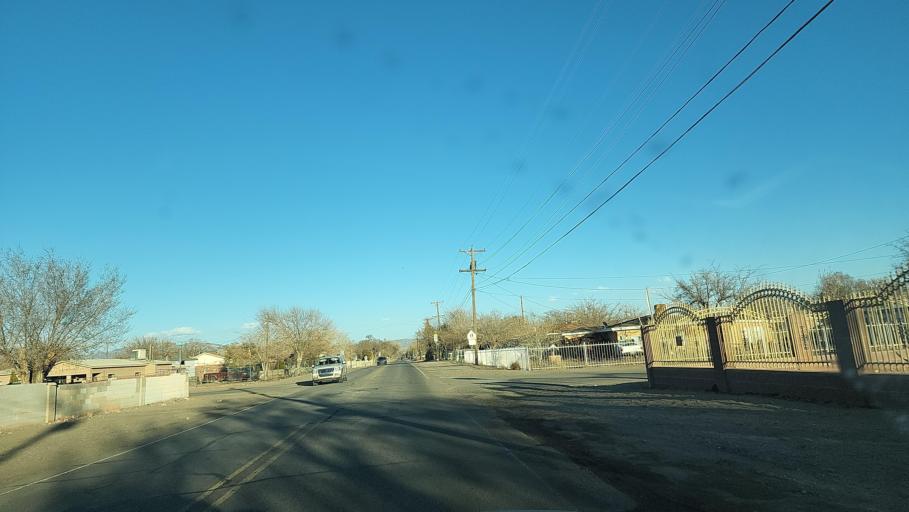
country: US
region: New Mexico
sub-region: Bernalillo County
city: South Valley
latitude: 35.0305
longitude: -106.7116
